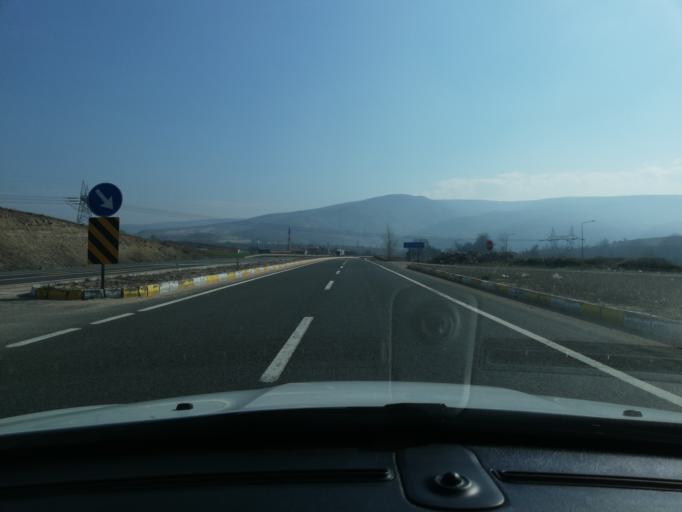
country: TR
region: Cankiri
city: Cerkes
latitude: 40.8399
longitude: 32.7542
